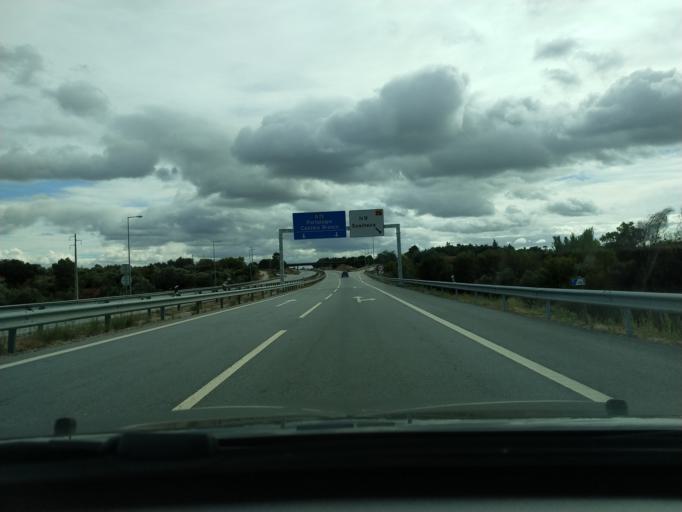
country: PT
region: Castelo Branco
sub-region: Concelho do Fundao
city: Fundao
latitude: 40.0324
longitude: -7.4685
